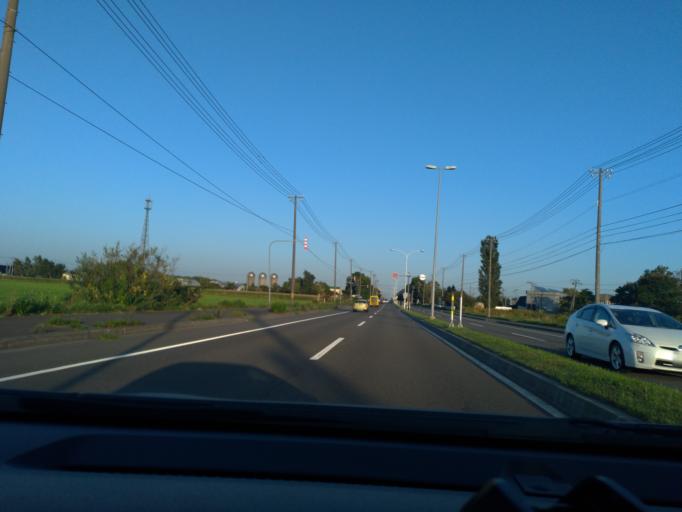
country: JP
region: Hokkaido
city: Ishikari
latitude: 43.1605
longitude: 141.3713
